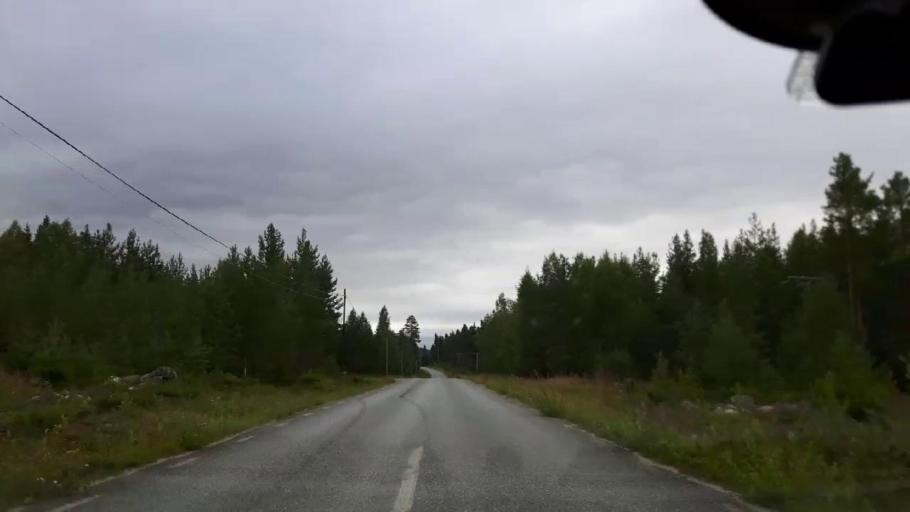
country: SE
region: Jaemtland
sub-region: Braecke Kommun
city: Braecke
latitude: 62.8816
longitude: 15.6182
